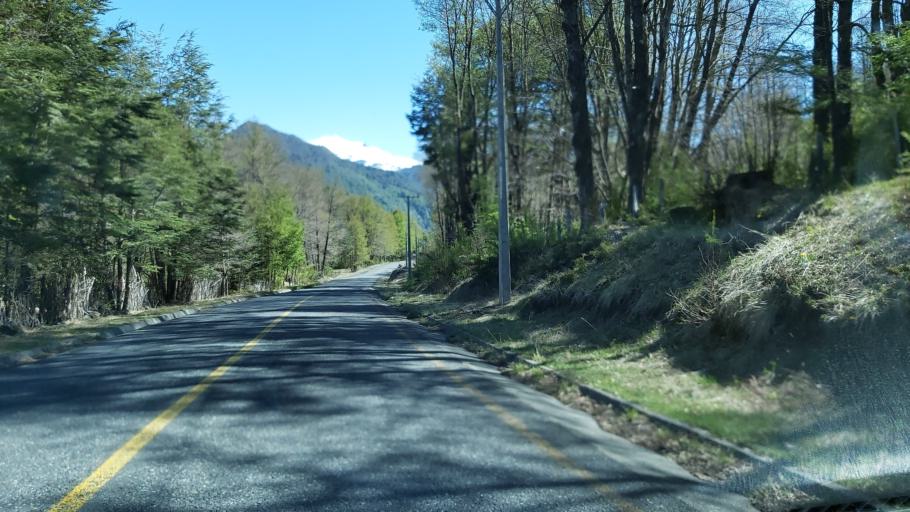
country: CL
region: Araucania
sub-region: Provincia de Cautin
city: Vilcun
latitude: -38.4645
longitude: -71.5184
